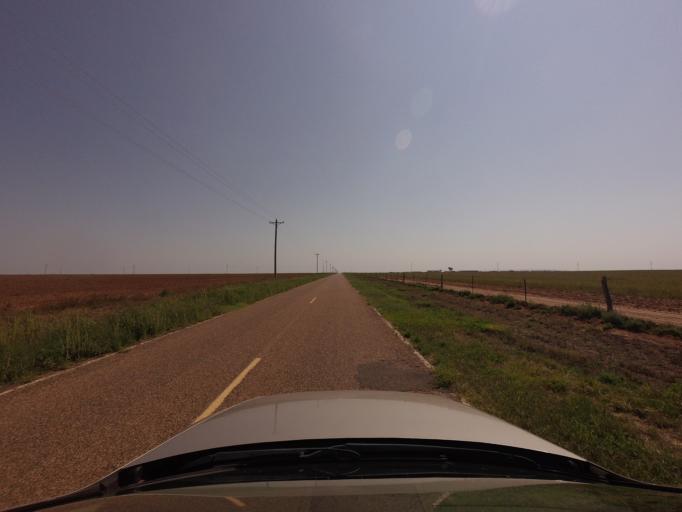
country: US
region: New Mexico
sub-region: Curry County
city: Cannon Air Force Base
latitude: 34.6329
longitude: -103.3418
